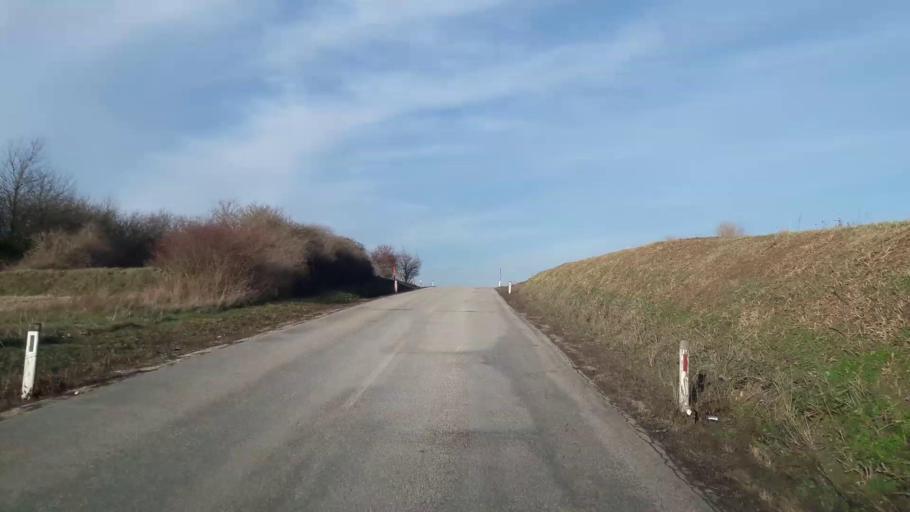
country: AT
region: Lower Austria
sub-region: Politischer Bezirk Ganserndorf
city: Gross-Schweinbarth
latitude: 48.4015
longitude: 16.6337
